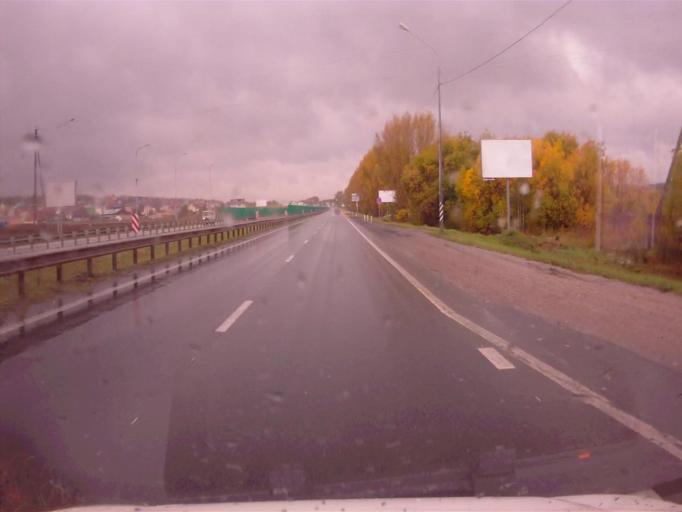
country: RU
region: Chelyabinsk
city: Dolgoderevenskoye
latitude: 55.2776
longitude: 61.3436
